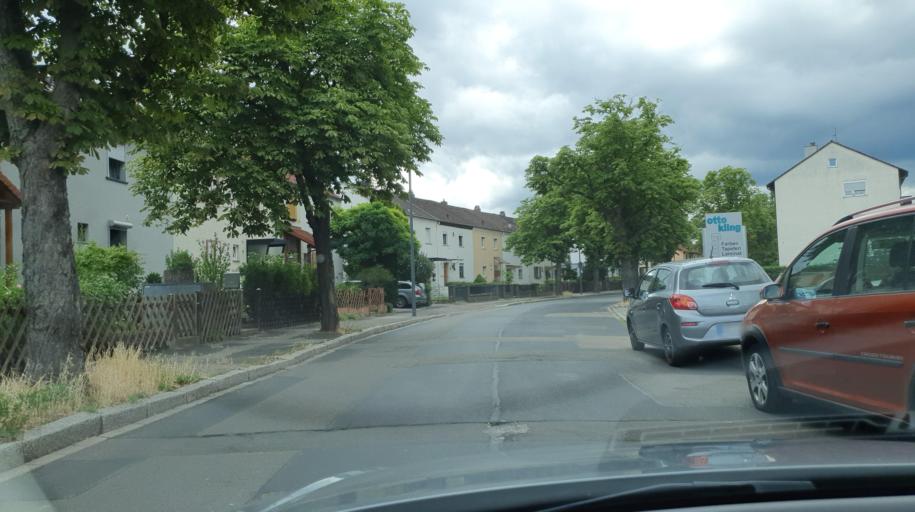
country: DE
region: Rheinland-Pfalz
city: Neustadt
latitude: 49.3515
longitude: 8.1569
